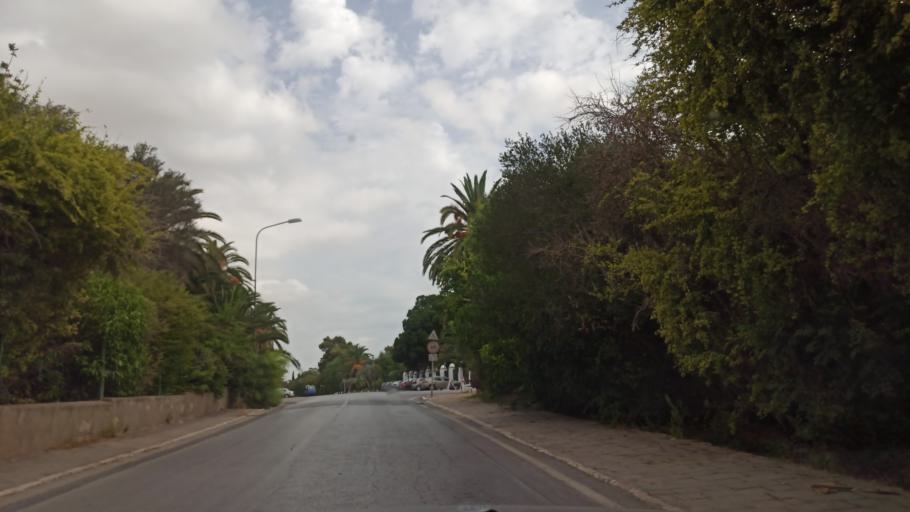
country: TN
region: Tunis
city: Tunis
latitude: 36.8206
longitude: 10.1745
